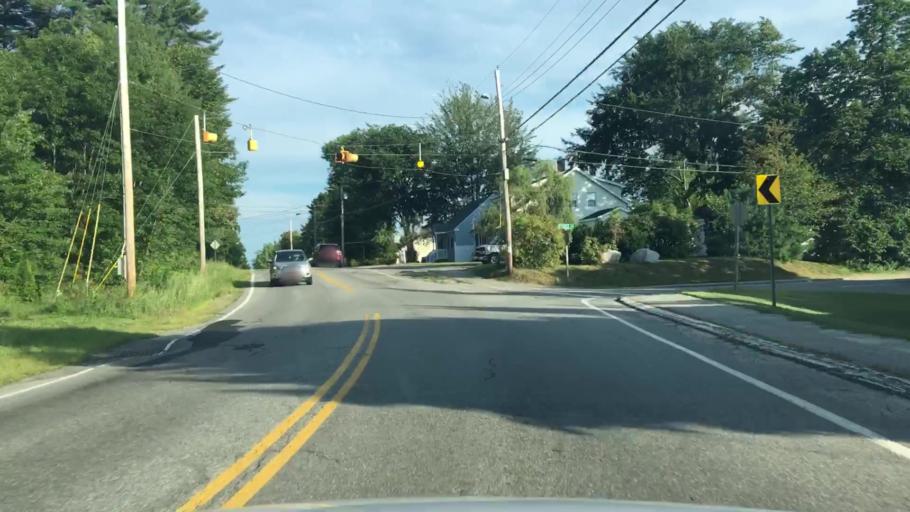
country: US
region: Maine
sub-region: Cumberland County
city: Westbrook
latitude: 43.6917
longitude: -70.3670
